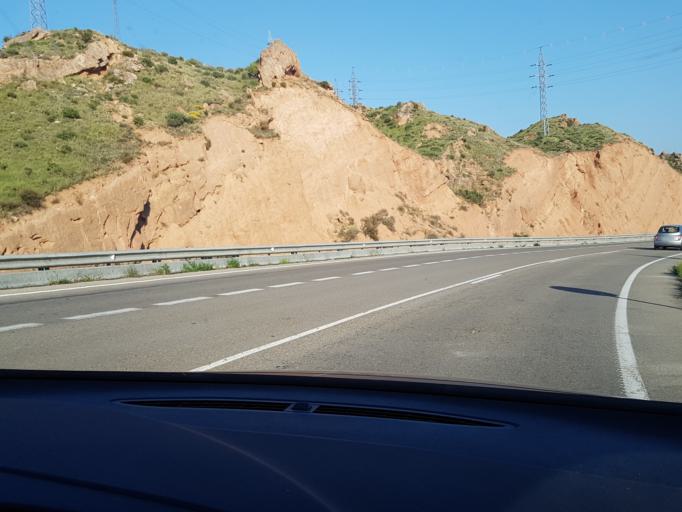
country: ES
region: La Rioja
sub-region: Provincia de La Rioja
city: Arnedo
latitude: 42.2389
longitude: -2.0867
